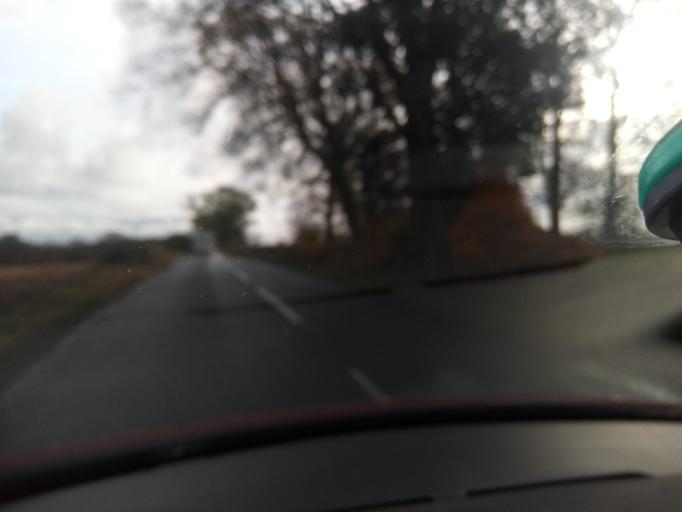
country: GB
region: England
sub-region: Northumberland
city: Birtley
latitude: 55.0723
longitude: -2.2021
